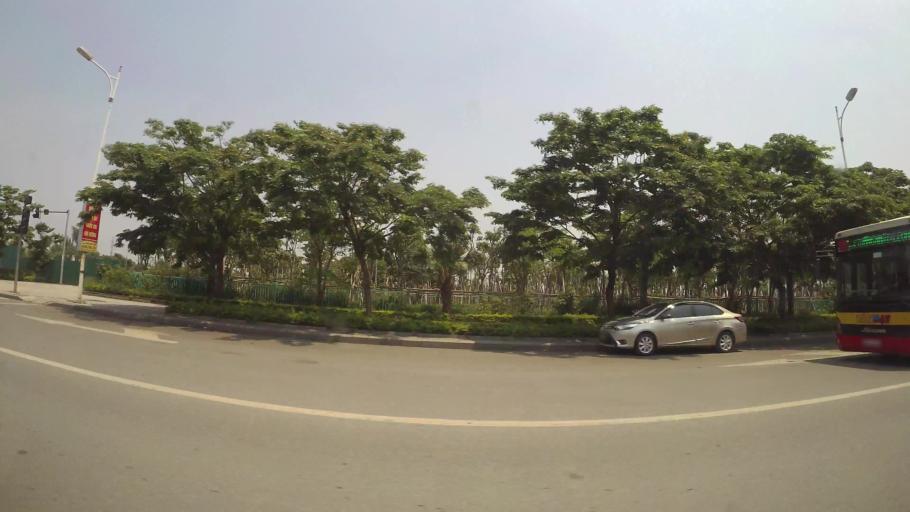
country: VN
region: Ha Noi
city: Trau Quy
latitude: 21.0314
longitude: 105.9002
